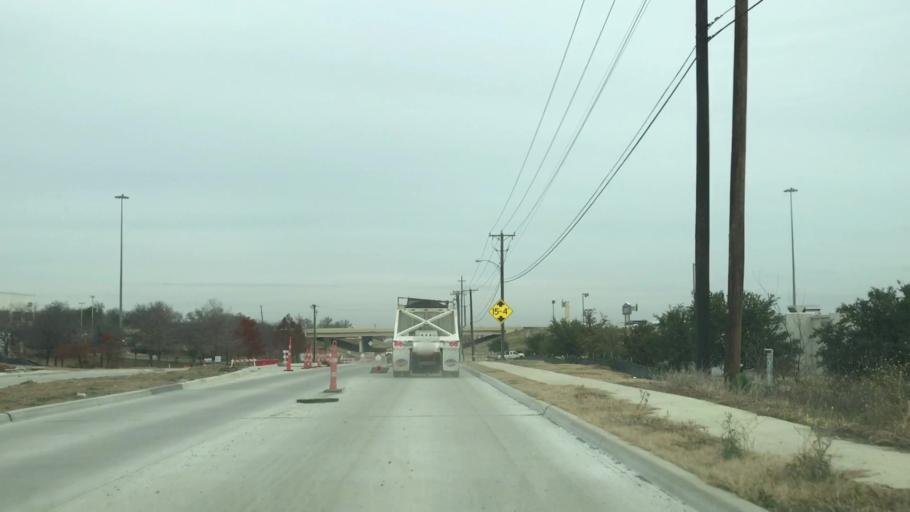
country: US
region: Texas
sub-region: Dallas County
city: Cockrell Hill
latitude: 32.7635
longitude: -96.9022
